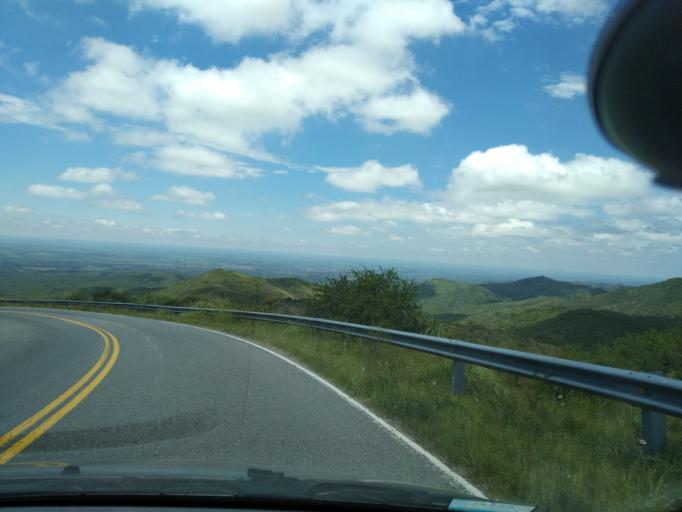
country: AR
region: Cordoba
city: Cuesta Blanca
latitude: -31.5959
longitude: -64.5328
